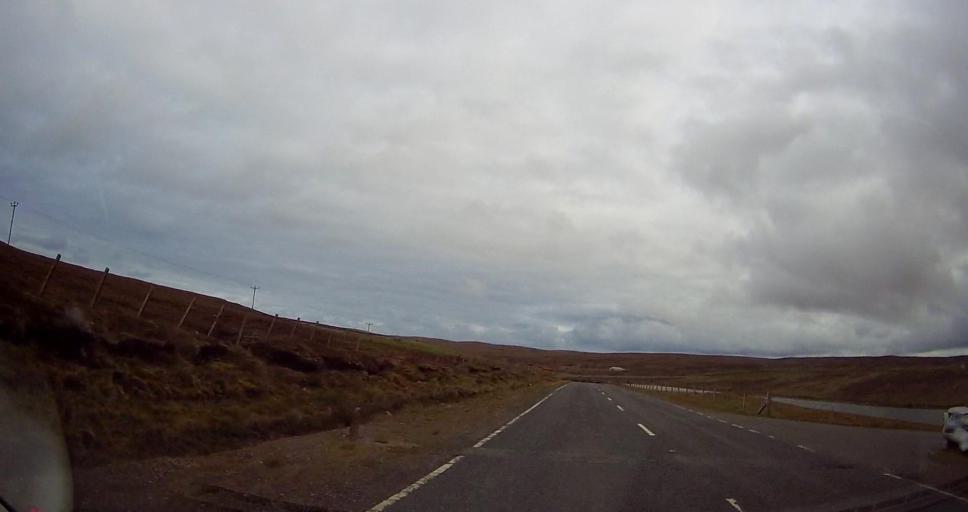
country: GB
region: Scotland
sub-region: Shetland Islands
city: Shetland
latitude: 60.6616
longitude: -1.0682
